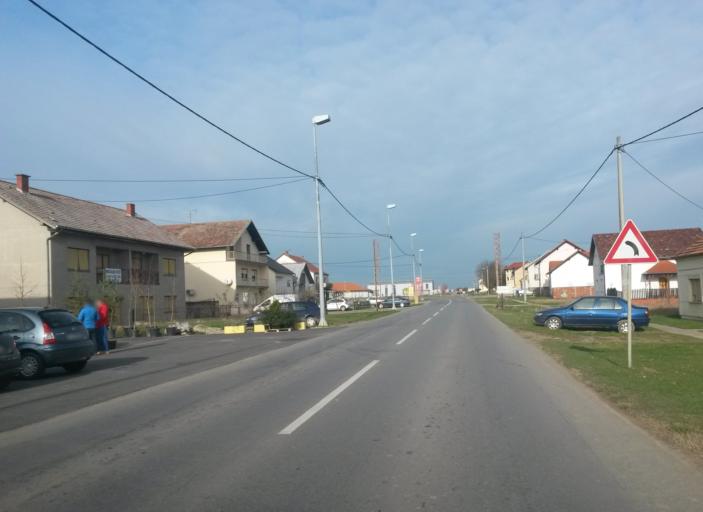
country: HR
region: Osjecko-Baranjska
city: Viskovci
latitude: 45.3329
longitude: 18.4200
